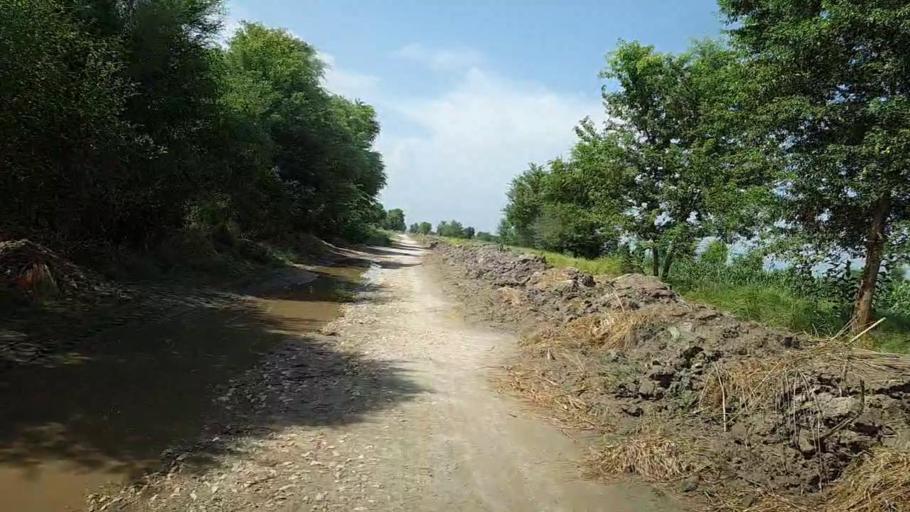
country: PK
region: Sindh
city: Bhiria
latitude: 26.8881
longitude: 68.2370
